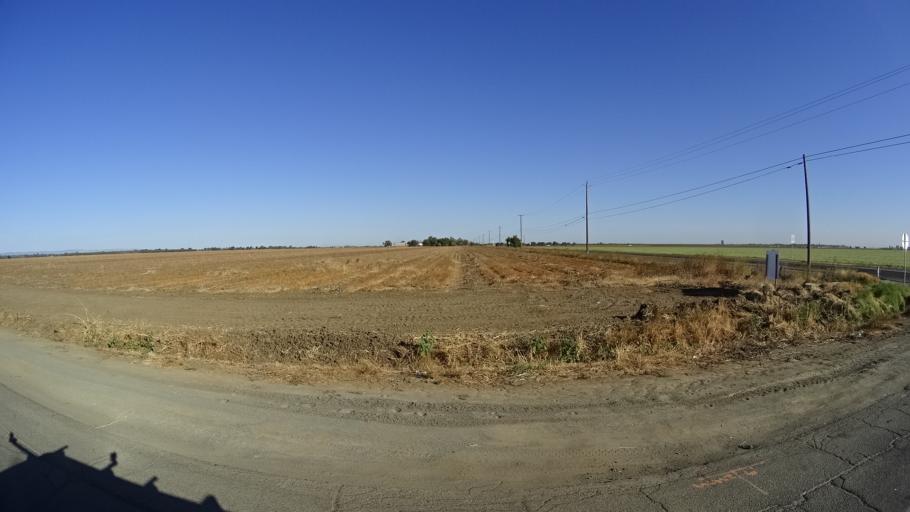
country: US
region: California
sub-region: Yolo County
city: Davis
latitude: 38.5613
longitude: -121.8042
